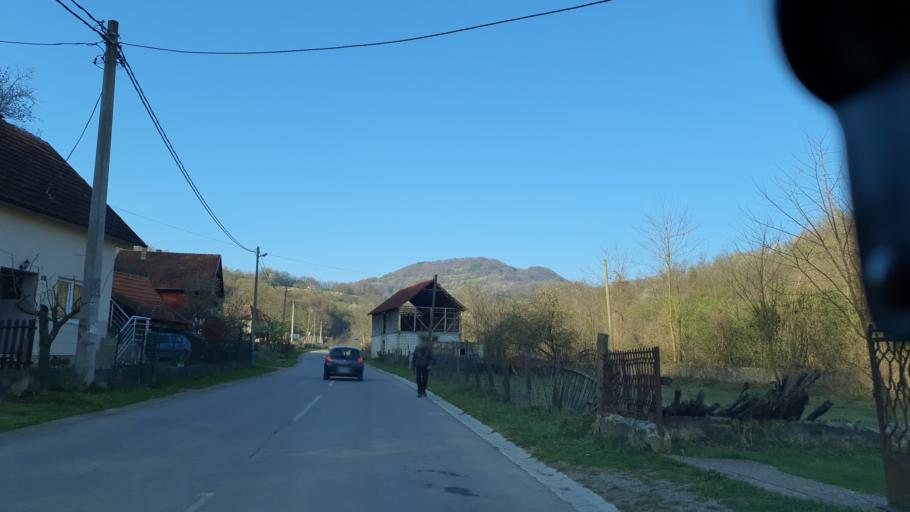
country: RS
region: Central Serbia
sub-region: Kolubarski Okrug
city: Osecina
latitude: 44.2887
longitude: 19.5367
